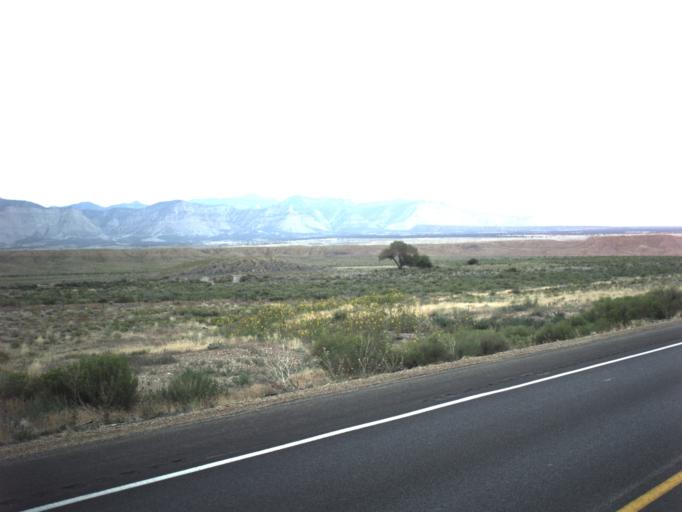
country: US
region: Utah
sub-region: Carbon County
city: East Carbon City
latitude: 39.4713
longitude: -110.4994
